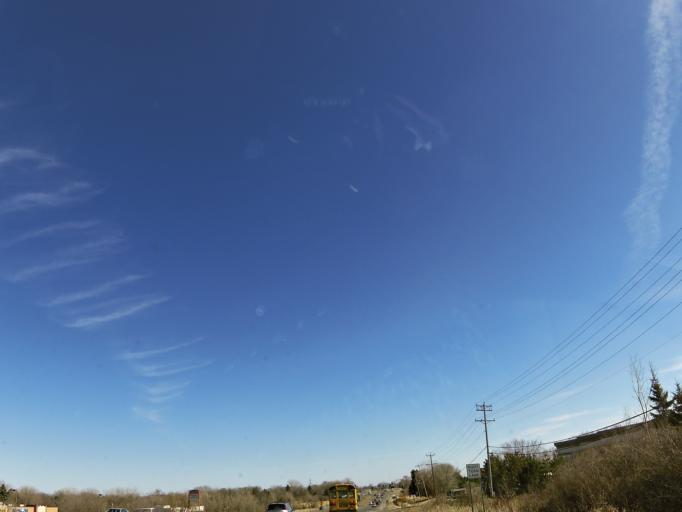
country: US
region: Minnesota
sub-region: Hennepin County
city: Plymouth
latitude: 45.0179
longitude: -93.4781
